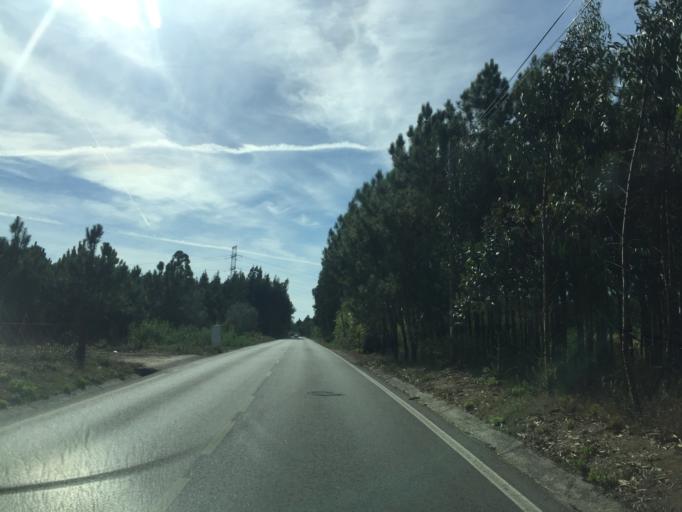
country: PT
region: Coimbra
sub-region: Figueira da Foz
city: Lavos
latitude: 40.0800
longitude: -8.8235
